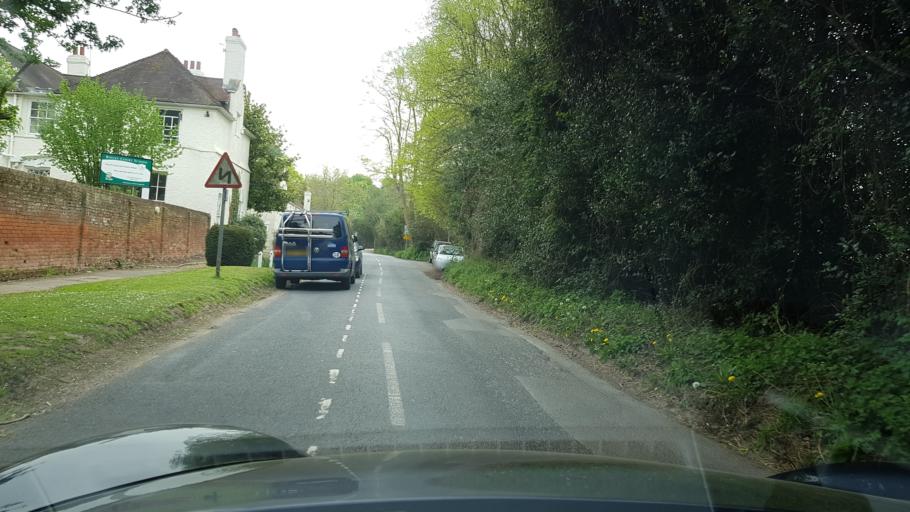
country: GB
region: England
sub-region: Surrey
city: Ripley
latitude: 51.2985
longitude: -0.4910
